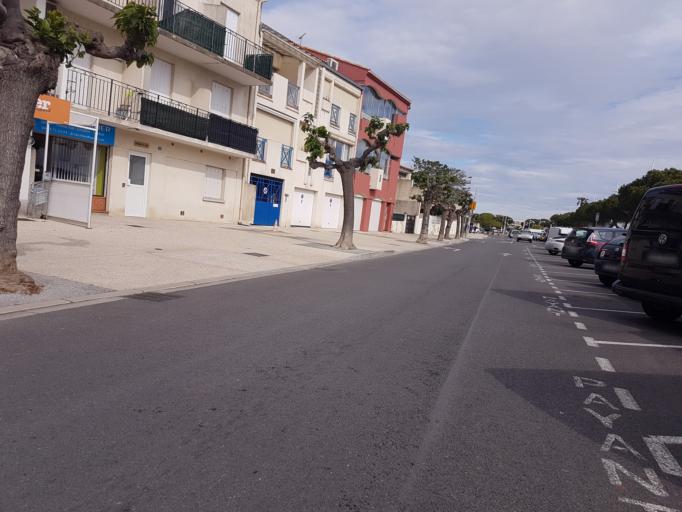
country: FR
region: Languedoc-Roussillon
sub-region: Departement du Gard
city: Le Grau-du-Roi
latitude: 43.5387
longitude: 4.1372
